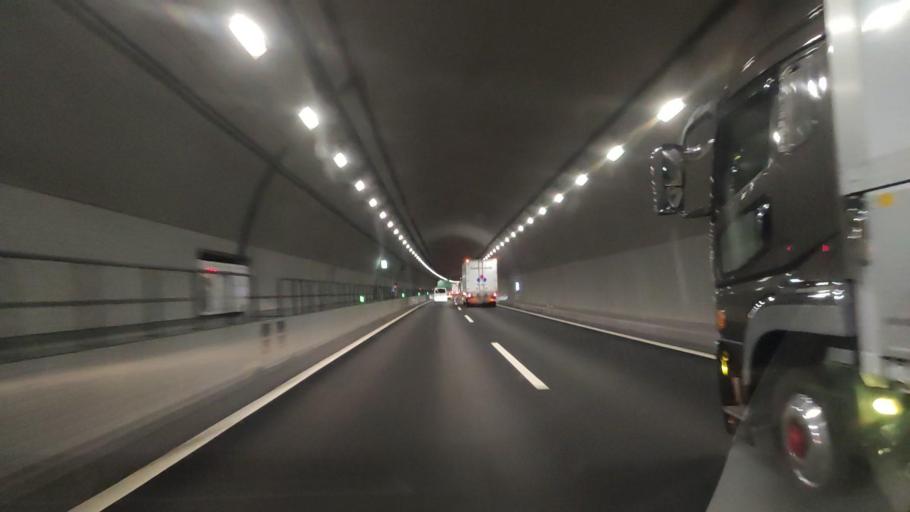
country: JP
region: Tokyo
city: Hachioji
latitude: 35.5678
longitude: 139.3064
